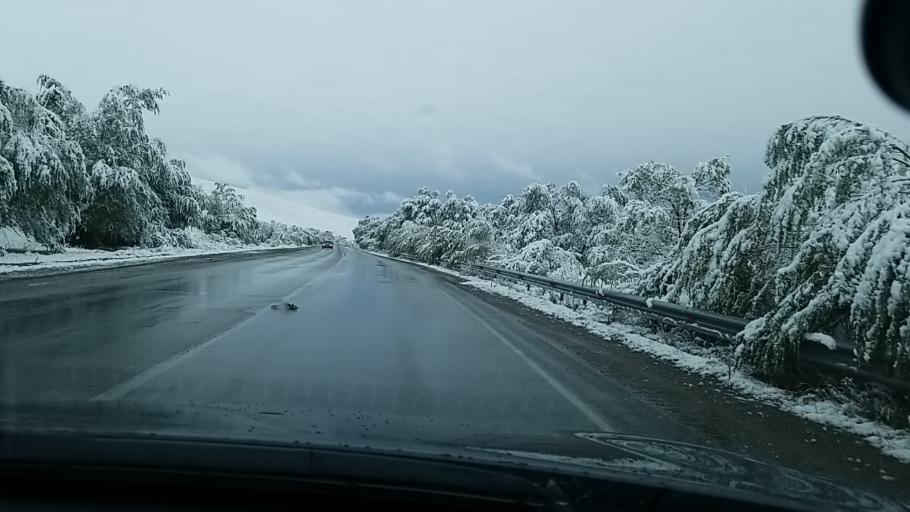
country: KZ
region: Almaty Oblysy
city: Burunday
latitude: 43.2904
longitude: 76.2448
